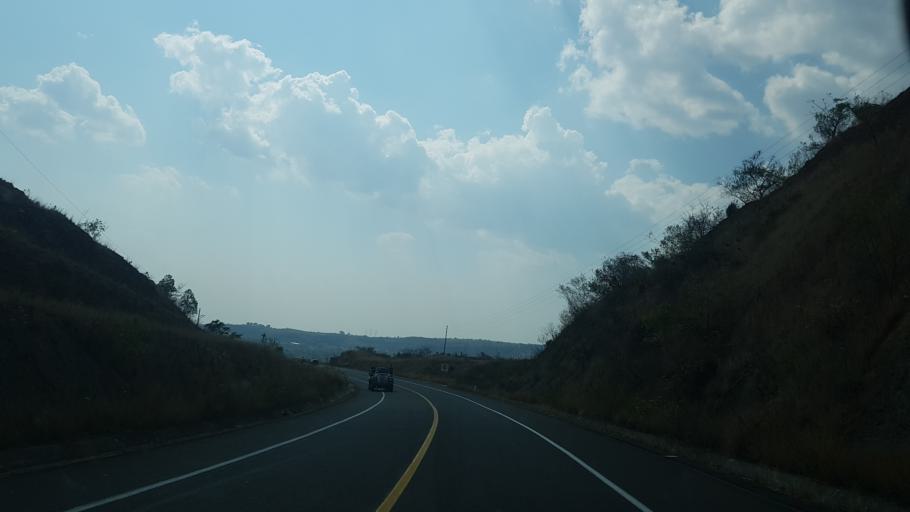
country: MX
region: Puebla
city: San Juan Amecac
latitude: 18.8221
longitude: -98.6859
